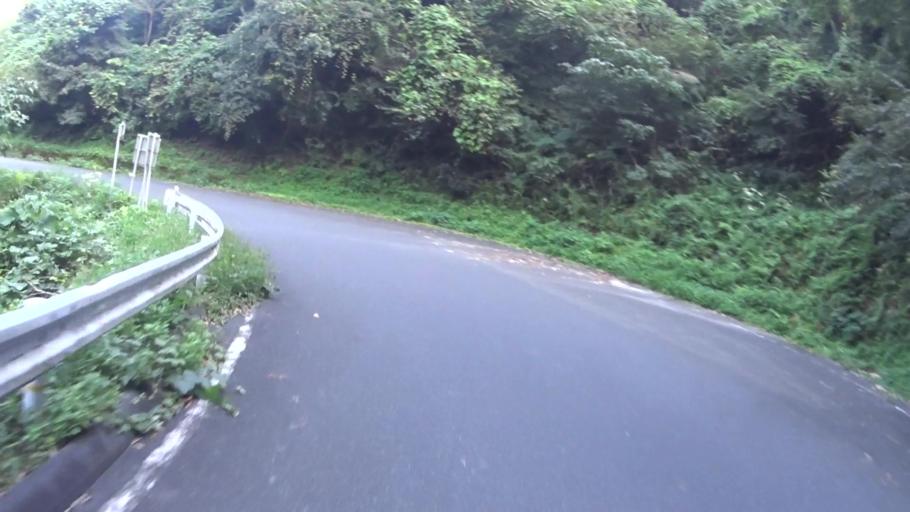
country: JP
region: Kyoto
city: Miyazu
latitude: 35.5681
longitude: 135.1389
